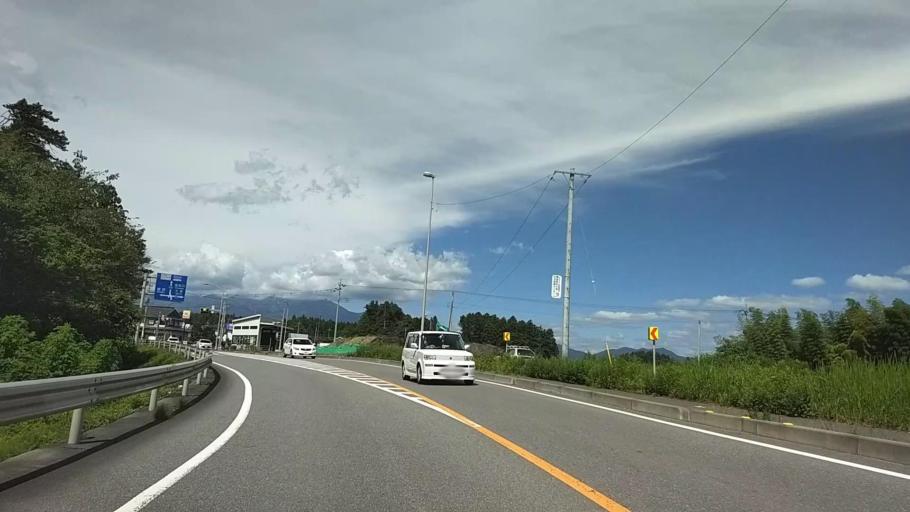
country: JP
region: Tochigi
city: Imaichi
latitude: 36.7061
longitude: 139.7482
